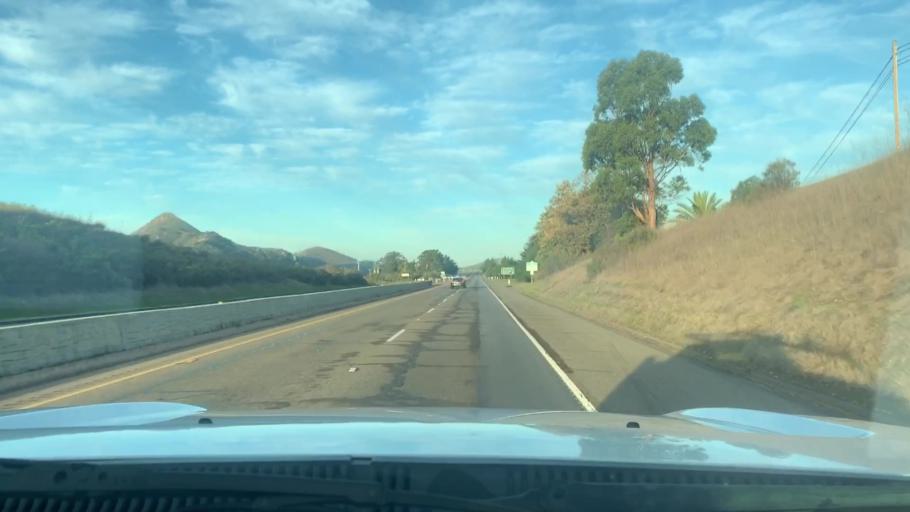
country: US
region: California
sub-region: San Luis Obispo County
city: Los Osos
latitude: 35.3538
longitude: -120.7811
